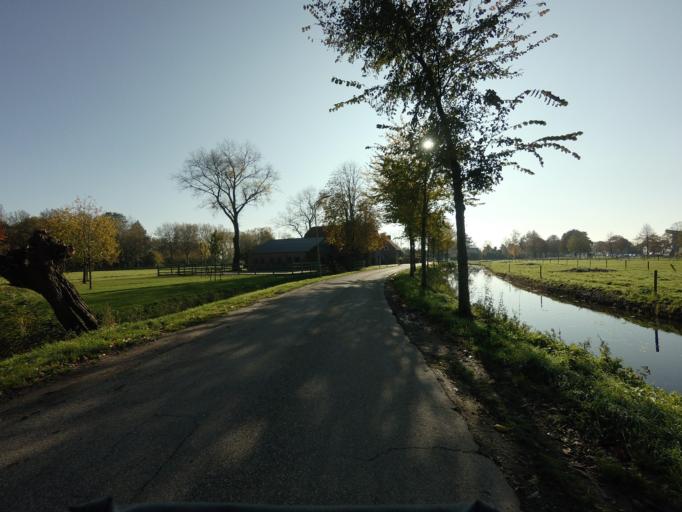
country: NL
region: North Brabant
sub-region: Gemeente Woudrichem
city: Almkerk
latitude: 51.7356
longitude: 4.9660
